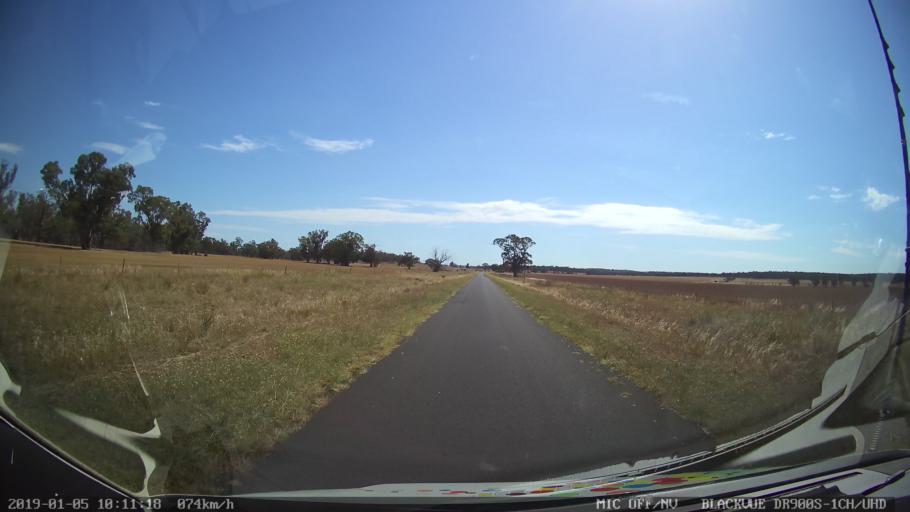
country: AU
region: New South Wales
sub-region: Gilgandra
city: Gilgandra
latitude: -31.6142
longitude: 148.8998
